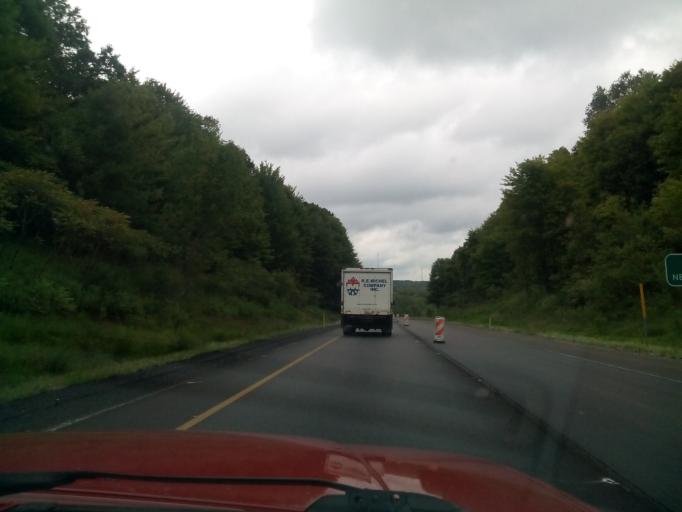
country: US
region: Pennsylvania
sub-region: Jefferson County
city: Falls Creek
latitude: 41.1550
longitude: -78.8374
